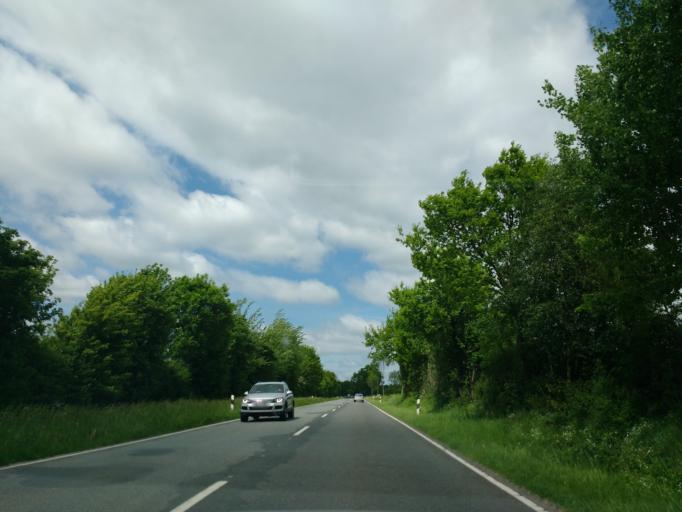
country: DE
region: Schleswig-Holstein
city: Stapelfeld
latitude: 53.5791
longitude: 10.2449
